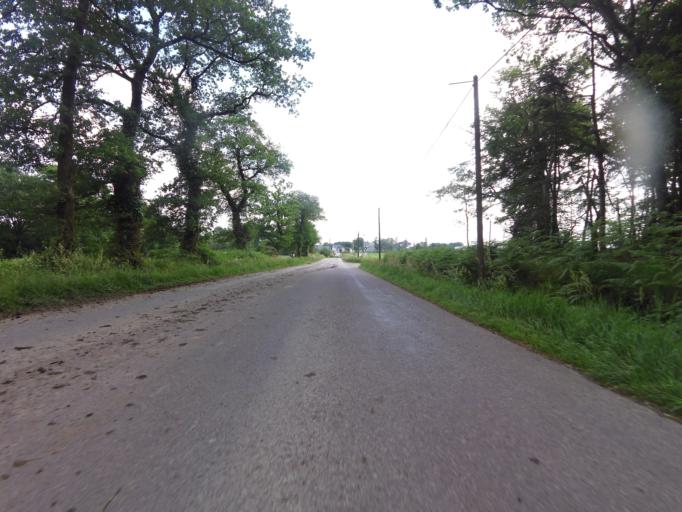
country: FR
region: Brittany
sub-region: Departement du Morbihan
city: Malansac
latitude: 47.6843
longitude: -2.3022
